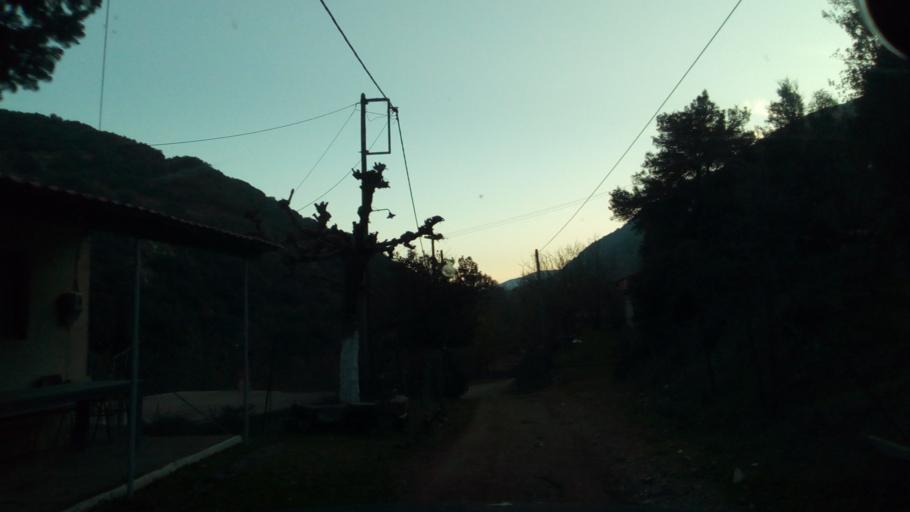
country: GR
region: West Greece
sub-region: Nomos Aitolias kai Akarnanias
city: Nafpaktos
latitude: 38.4684
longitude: 21.8134
